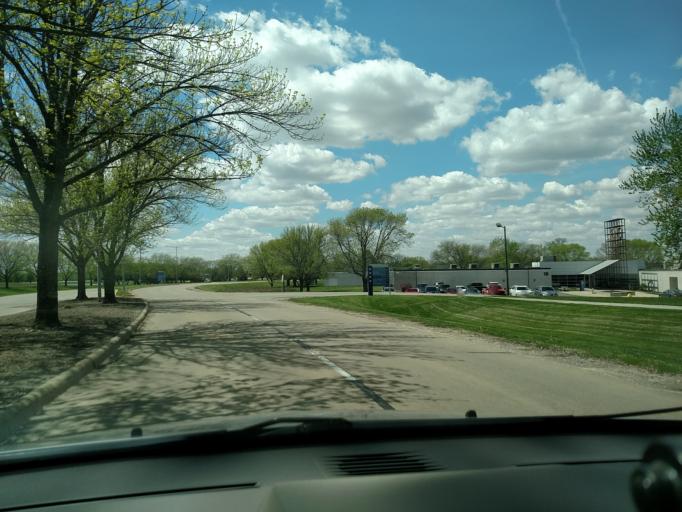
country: US
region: Iowa
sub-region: Polk County
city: Ankeny
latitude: 41.7087
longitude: -93.6021
